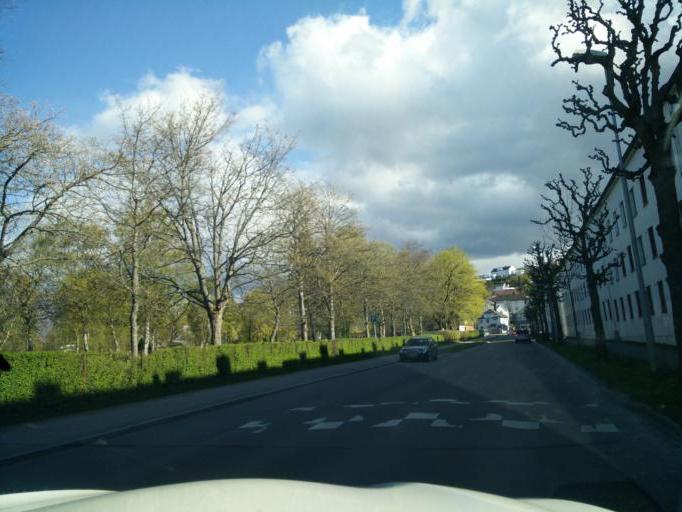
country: NO
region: Sor-Trondelag
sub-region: Trondheim
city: Trondheim
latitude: 63.4388
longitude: 10.4343
